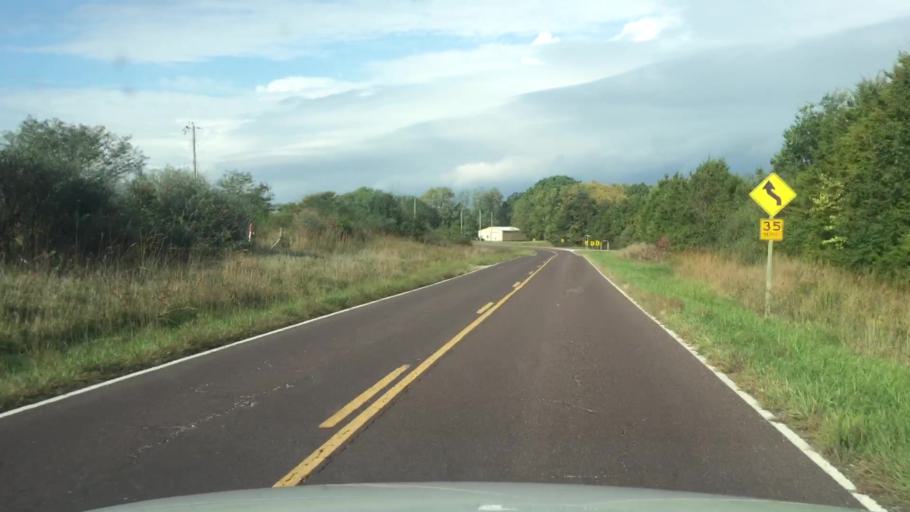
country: US
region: Missouri
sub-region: Boone County
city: Columbia
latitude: 38.8695
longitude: -92.2955
